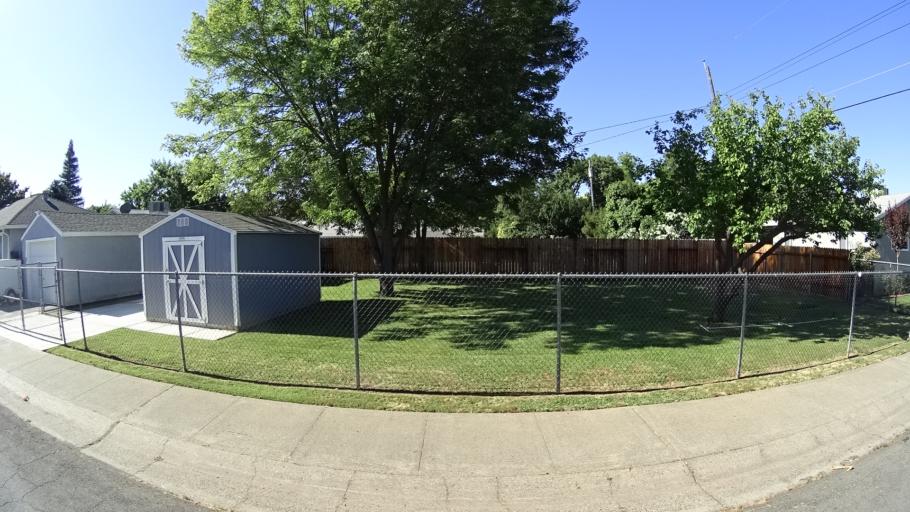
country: US
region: California
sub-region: Sacramento County
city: Florin
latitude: 38.5448
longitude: -121.4323
